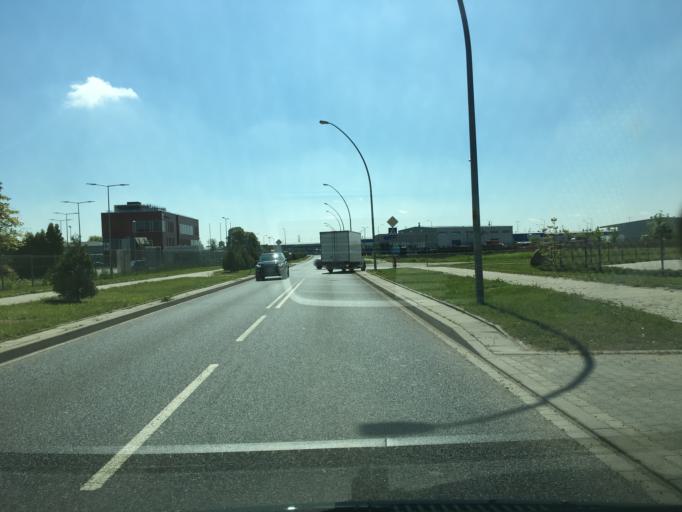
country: PL
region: Lower Silesian Voivodeship
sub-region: Powiat wroclawski
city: Bielany Wroclawskie
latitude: 51.0718
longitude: 16.9592
